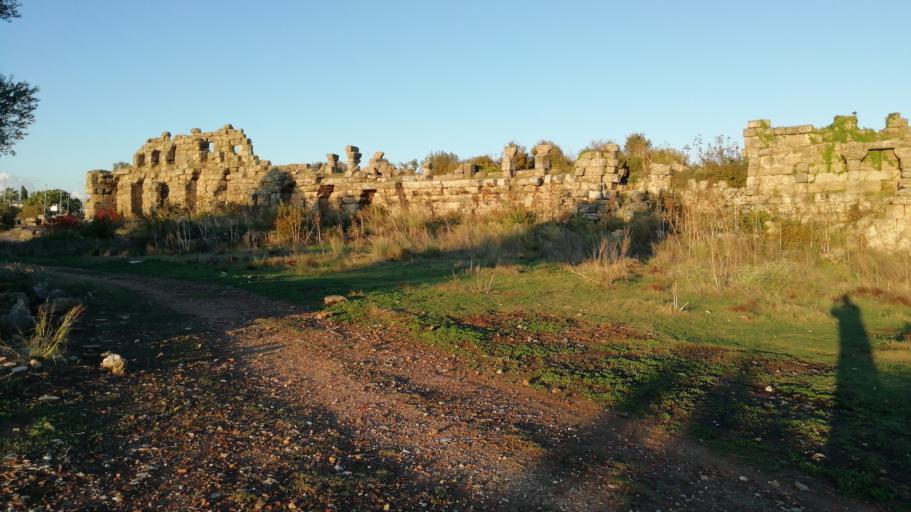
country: TR
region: Antalya
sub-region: Manavgat
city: Side
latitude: 36.7701
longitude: 31.3945
